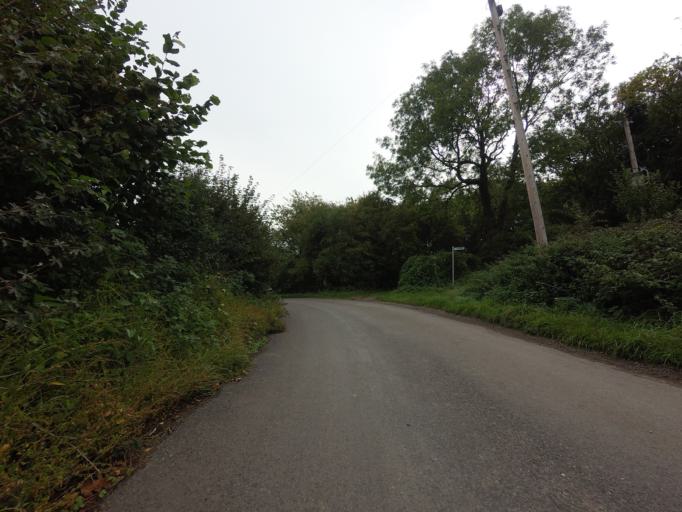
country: GB
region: England
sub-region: Hertfordshire
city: Reed
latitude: 51.9812
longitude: 0.0411
